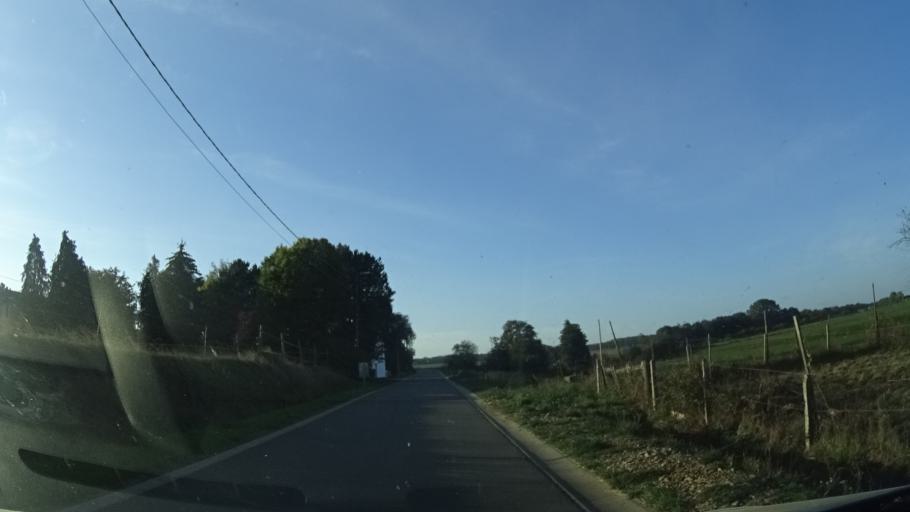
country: BE
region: Wallonia
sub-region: Province de Namur
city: Cerfontaine
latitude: 50.2112
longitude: 4.3591
